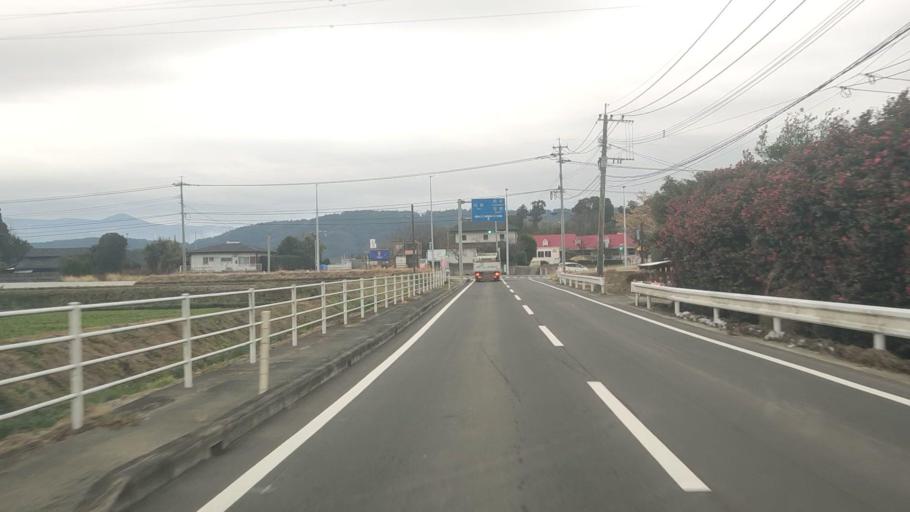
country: JP
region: Kumamoto
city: Ozu
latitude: 32.8660
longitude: 130.8906
